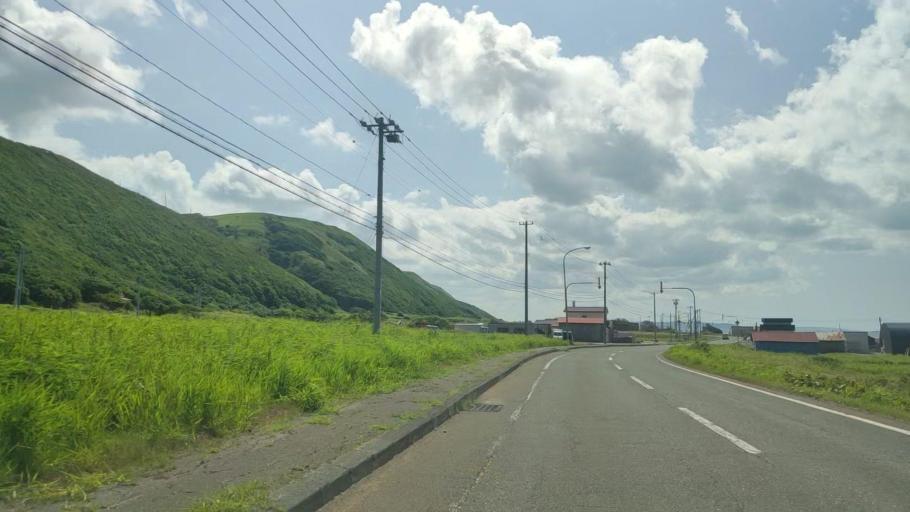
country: JP
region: Hokkaido
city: Wakkanai
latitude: 45.4078
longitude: 141.6362
